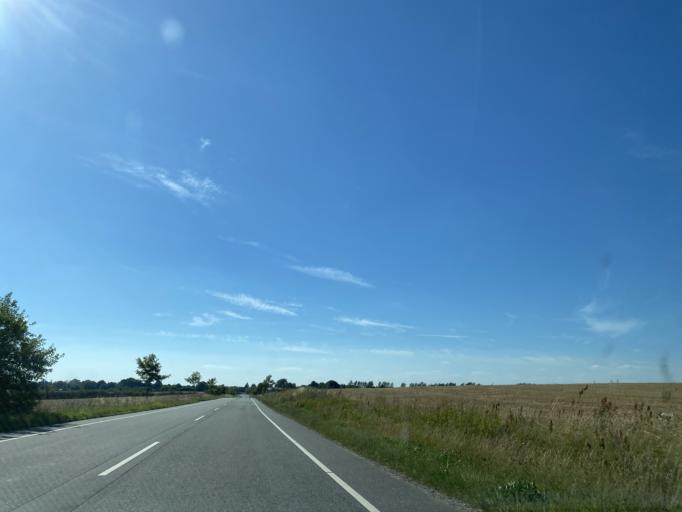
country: DK
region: Central Jutland
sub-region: Hedensted Kommune
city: Torring
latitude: 55.8671
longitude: 9.3772
